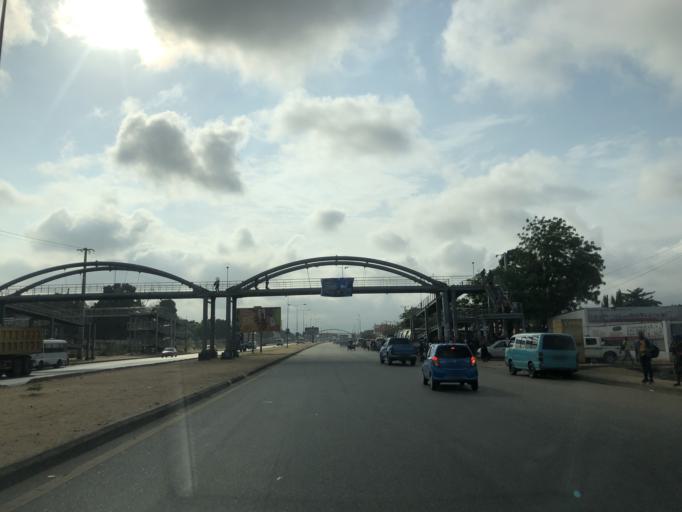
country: AO
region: Luanda
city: Luanda
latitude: -8.9145
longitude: 13.3890
